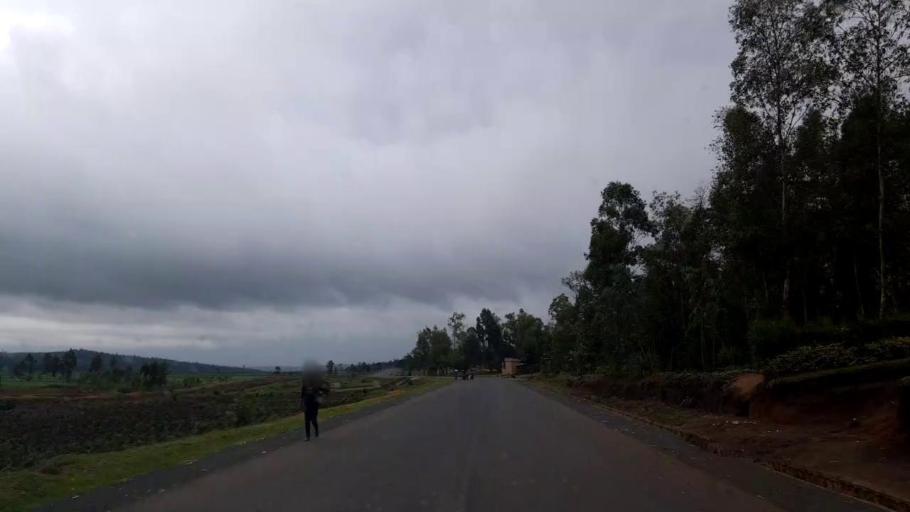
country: RW
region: Northern Province
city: Byumba
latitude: -1.4441
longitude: 30.2512
